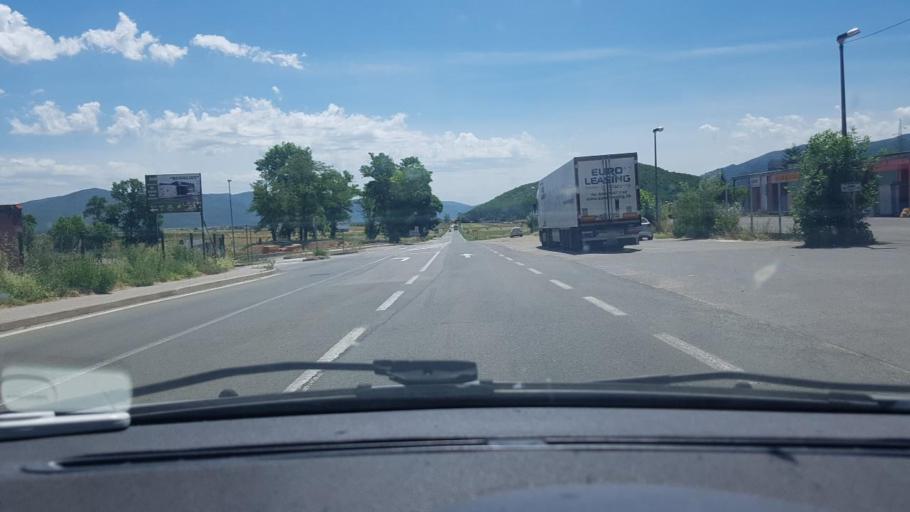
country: HR
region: Licko-Senjska
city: Otocac
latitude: 44.8611
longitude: 15.2640
